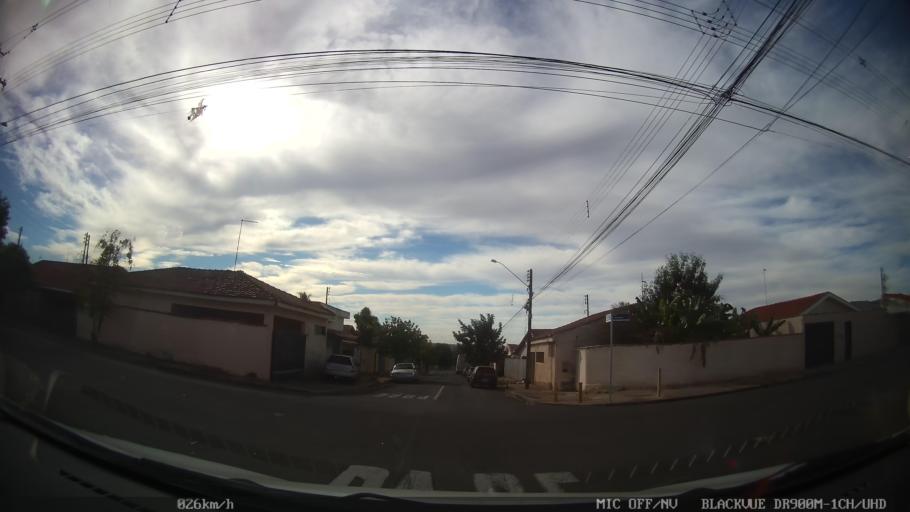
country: BR
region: Sao Paulo
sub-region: Catanduva
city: Catanduva
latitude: -21.1260
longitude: -48.9997
